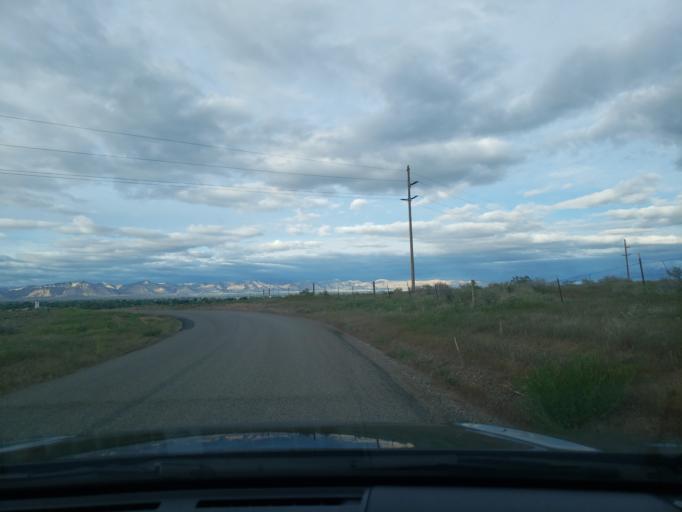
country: US
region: Colorado
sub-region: Mesa County
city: Fruita
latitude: 39.1403
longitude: -108.7498
